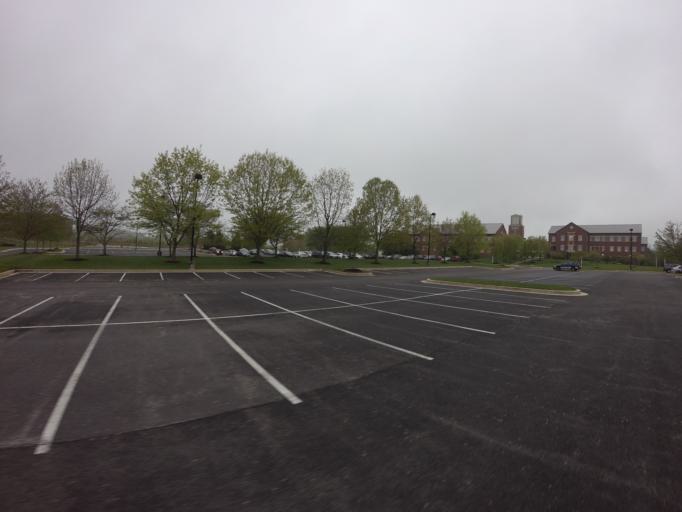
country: US
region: Maryland
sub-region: Baltimore County
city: Hunt Valley
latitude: 39.5271
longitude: -76.6541
